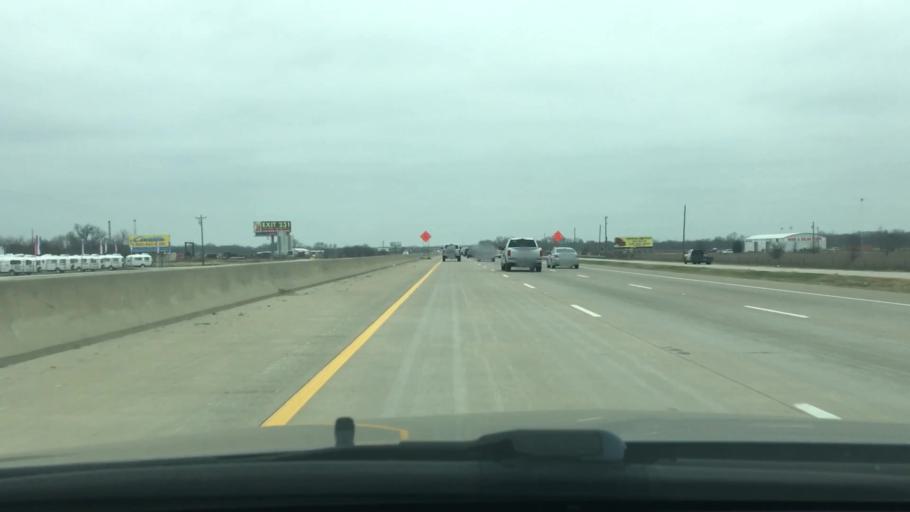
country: US
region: Texas
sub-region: Navarro County
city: Corsicana
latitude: 32.1913
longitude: -96.4728
